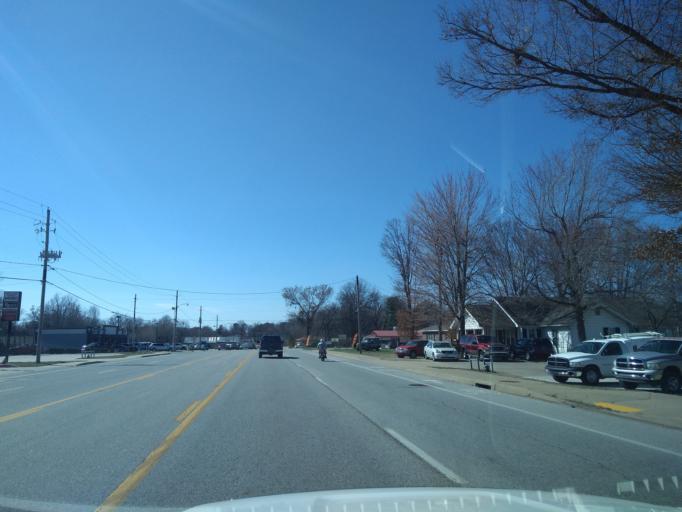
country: US
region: Arkansas
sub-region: Washington County
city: Farmington
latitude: 36.0420
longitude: -94.2436
